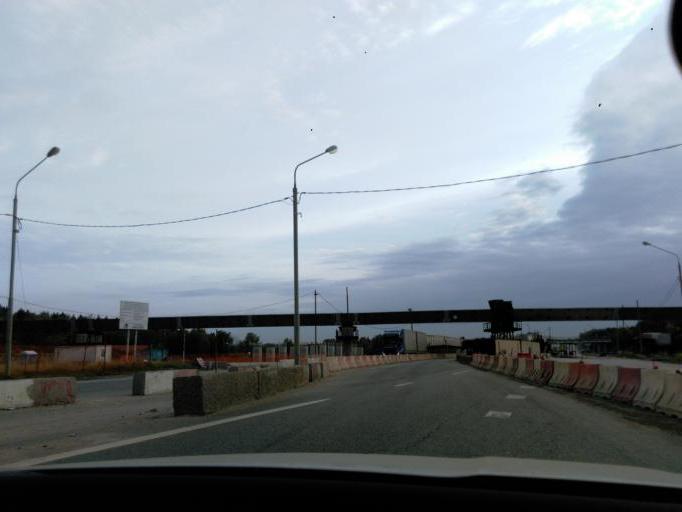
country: RU
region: Moskovskaya
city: Novopodrezkovo
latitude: 55.9705
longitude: 37.3739
